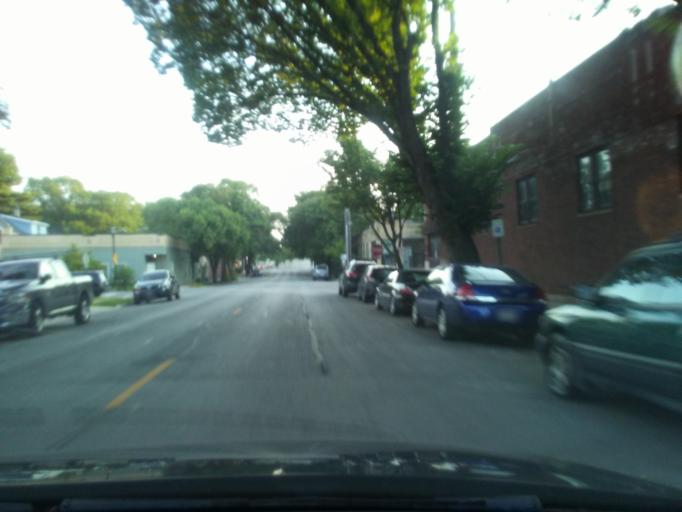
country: US
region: Illinois
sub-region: Cook County
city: Evanston
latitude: 42.0312
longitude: -87.6803
